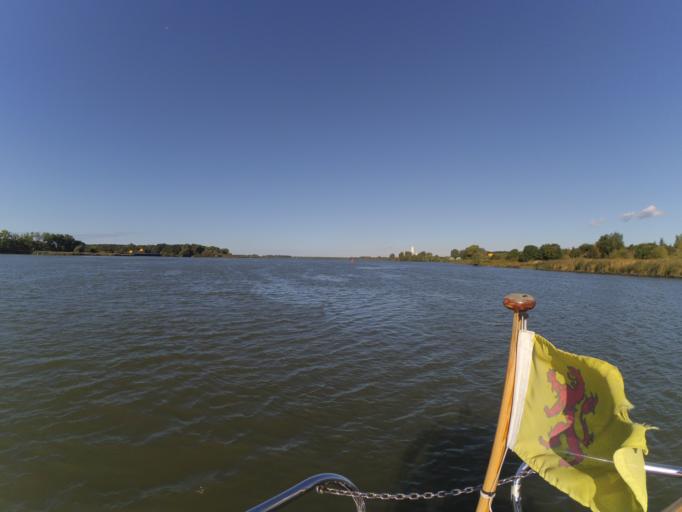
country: NL
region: South Holland
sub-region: Gemeente Barendrecht
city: Barendrecht
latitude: 51.8324
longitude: 4.5181
